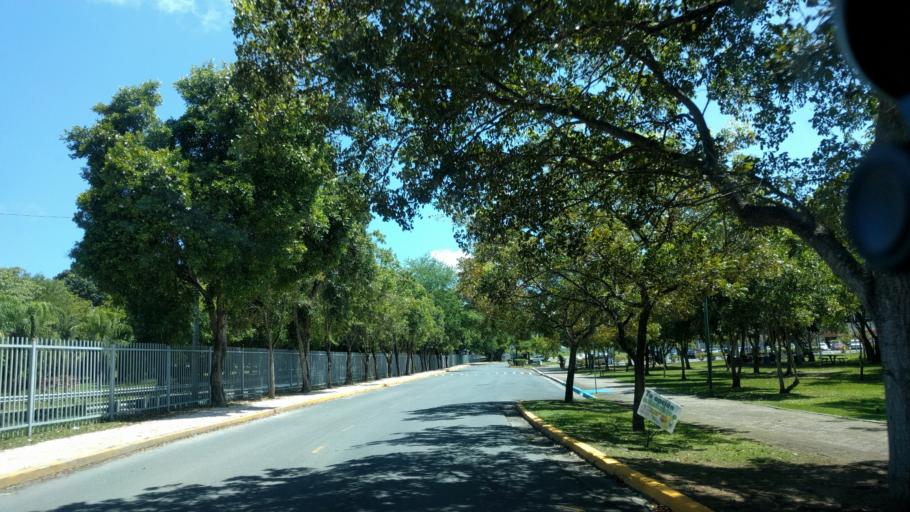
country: PR
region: San Juan
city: San Juan
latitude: 18.4417
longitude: -66.0796
